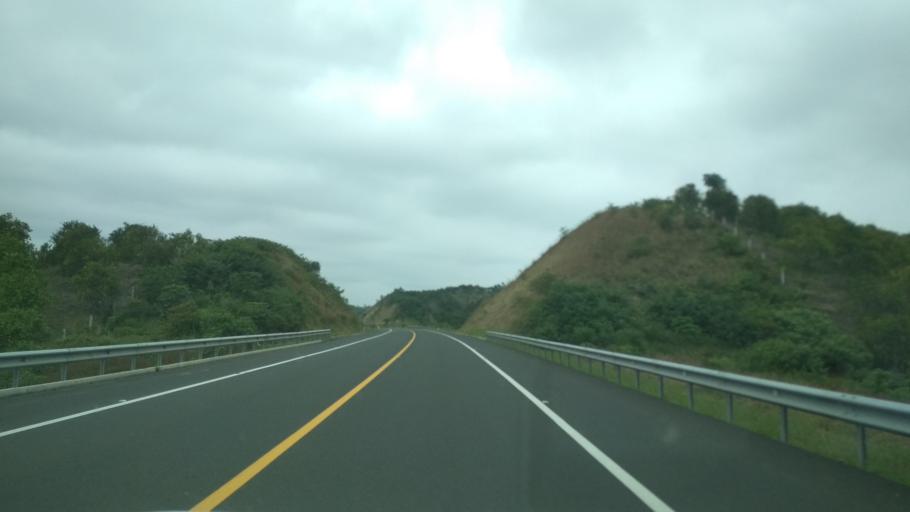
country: MX
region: Veracruz
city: Gutierrez Zamora
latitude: 20.2970
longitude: -97.0793
